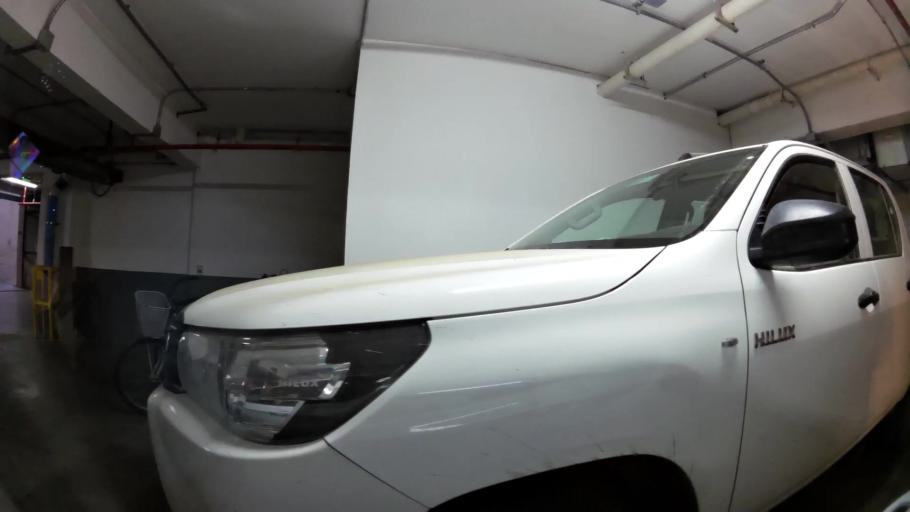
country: CL
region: Maule
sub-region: Provincia de Curico
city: Curico
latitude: -34.9859
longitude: -71.2330
